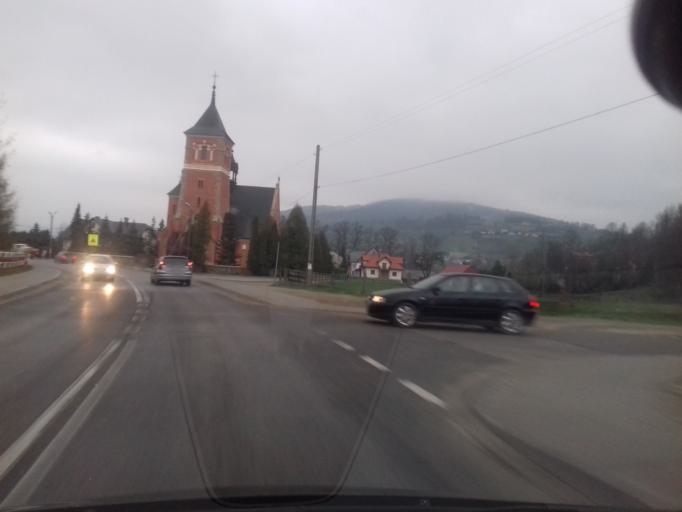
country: PL
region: Lesser Poland Voivodeship
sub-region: Powiat limanowski
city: Mszana Dolna
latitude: 49.7025
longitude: 20.0376
